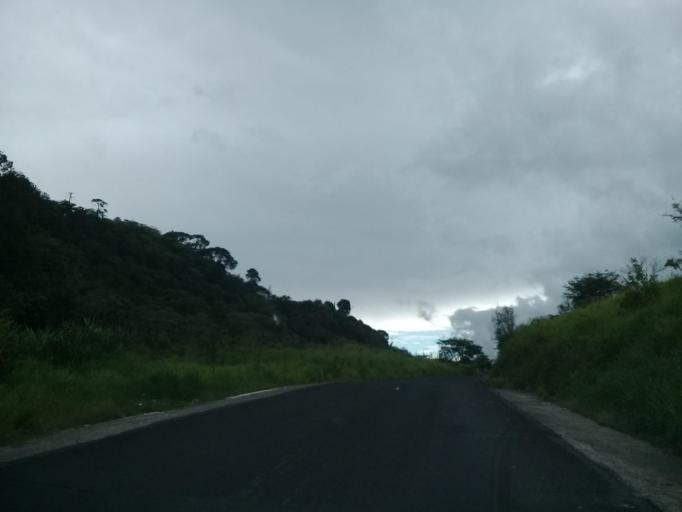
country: MX
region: Veracruz
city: El Castillo
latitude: 19.5574
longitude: -96.8422
